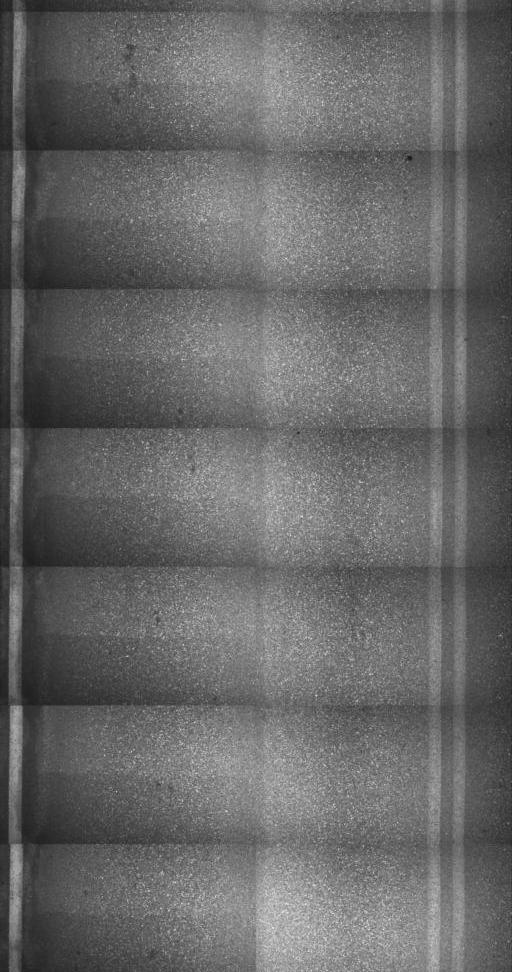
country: US
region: Vermont
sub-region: Lamoille County
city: Hyde Park
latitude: 44.6255
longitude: -72.5993
